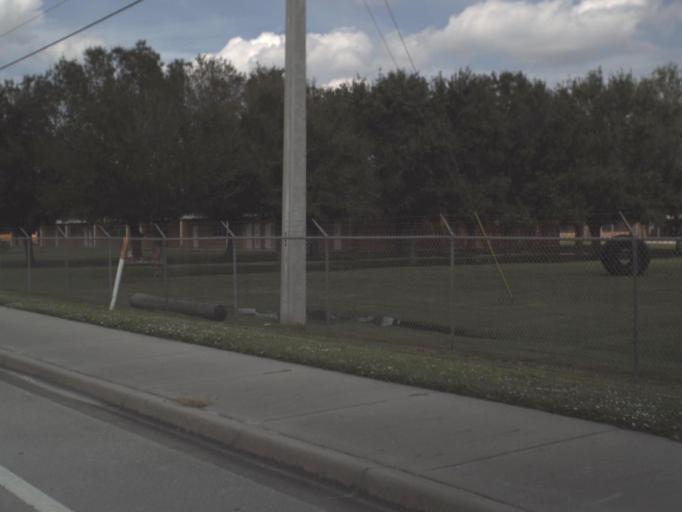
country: US
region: Florida
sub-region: Okeechobee County
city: Cypress Quarters
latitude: 27.2670
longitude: -80.8299
